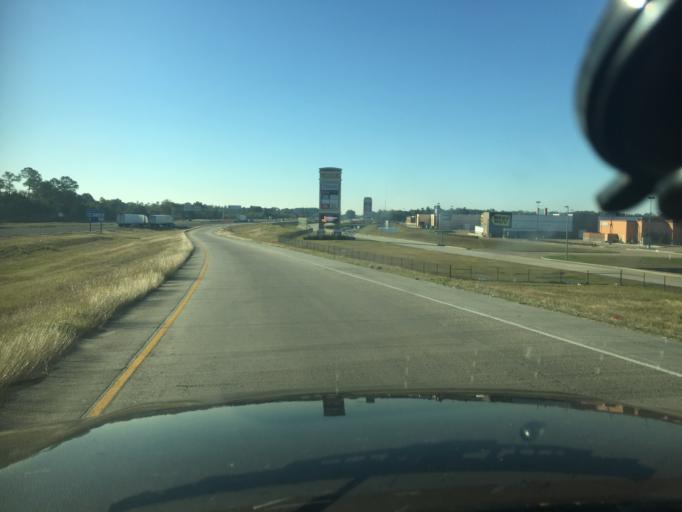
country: US
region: Louisiana
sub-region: Saint Tammany Parish
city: Slidell
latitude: 30.2701
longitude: -89.7562
